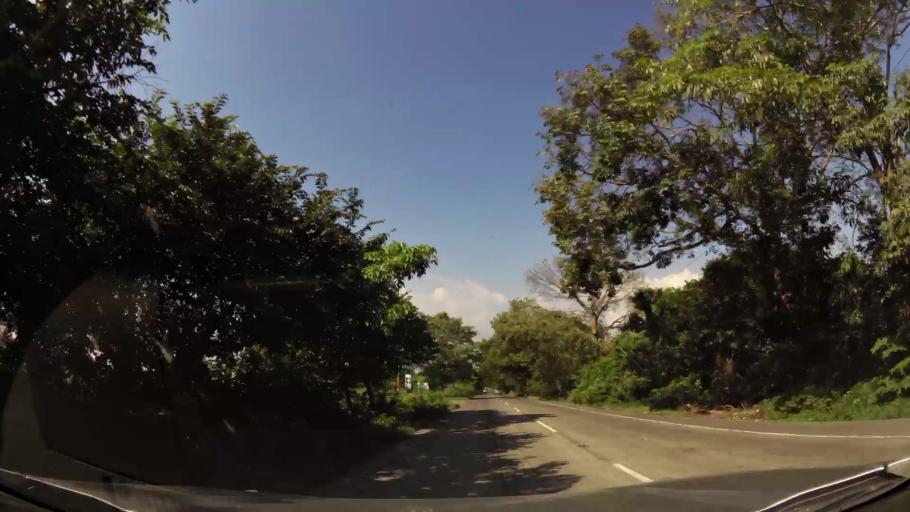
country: GT
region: Escuintla
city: Puerto San Jose
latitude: 13.9782
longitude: -90.7885
